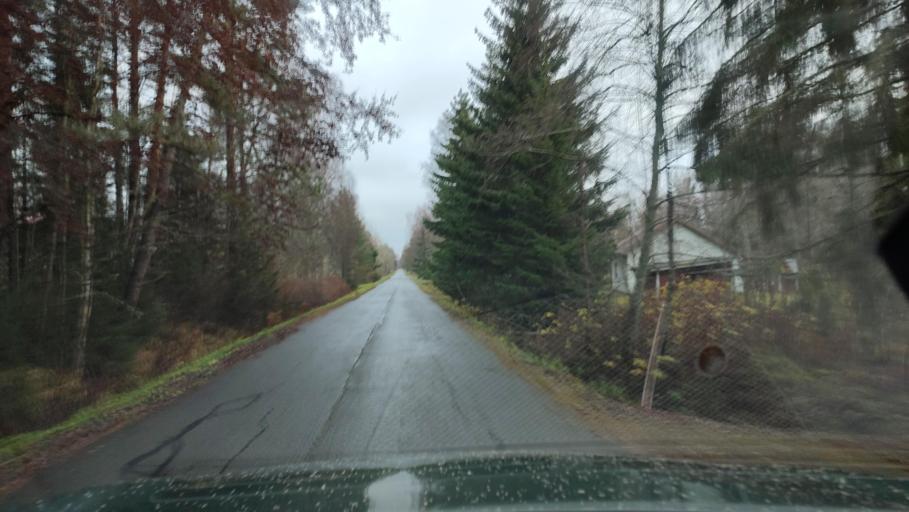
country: FI
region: Southern Ostrobothnia
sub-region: Suupohja
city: Teuva
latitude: 62.4573
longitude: 21.5907
